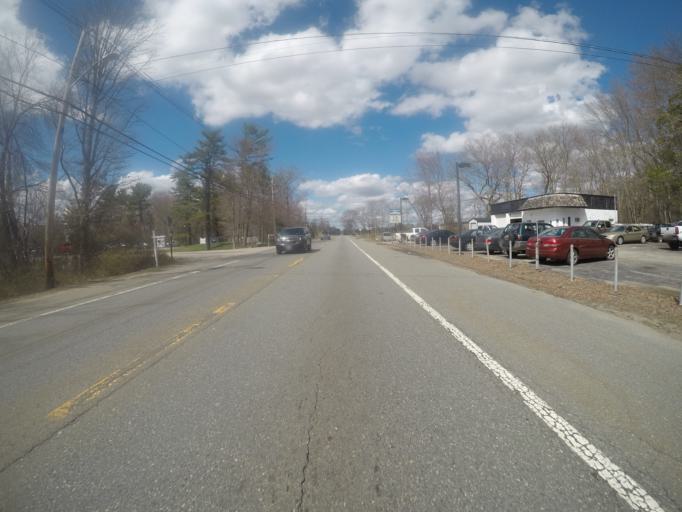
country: US
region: Massachusetts
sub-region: Bristol County
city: Raynham
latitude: 42.0032
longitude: -71.0669
